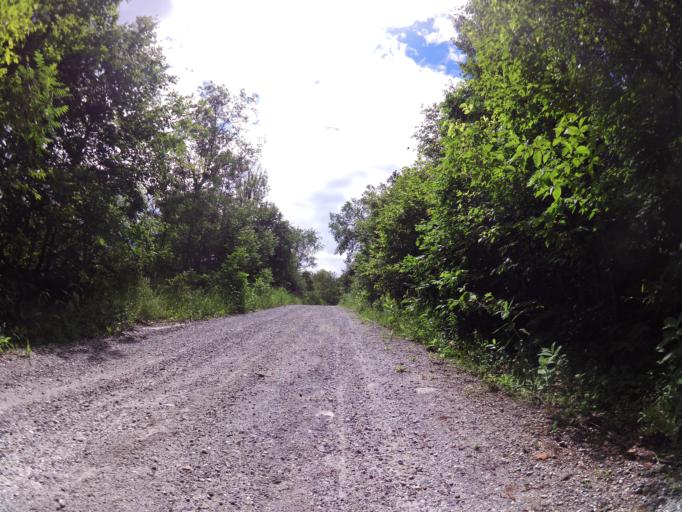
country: CA
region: Ontario
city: Perth
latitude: 45.0217
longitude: -76.5571
